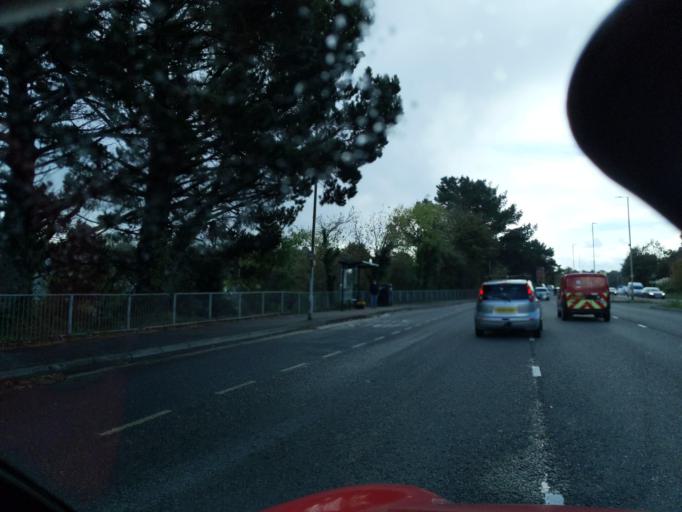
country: GB
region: England
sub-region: Devon
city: Plympton
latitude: 50.3891
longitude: -4.0886
